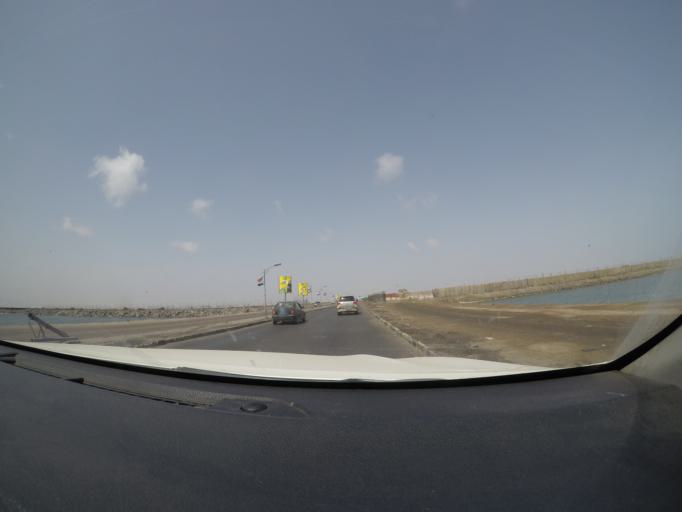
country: YE
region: Aden
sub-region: Khur Maksar
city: Khawr Maksar
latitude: 12.8292
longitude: 45.0308
